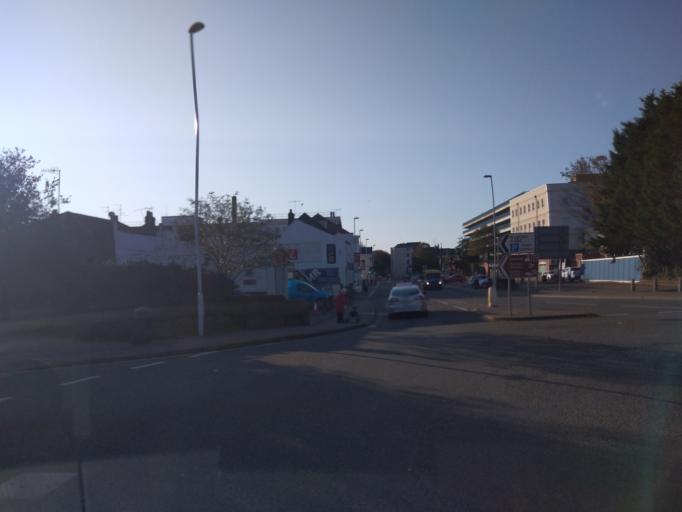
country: GB
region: England
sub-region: West Sussex
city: Worthing
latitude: 50.8142
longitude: -0.3681
